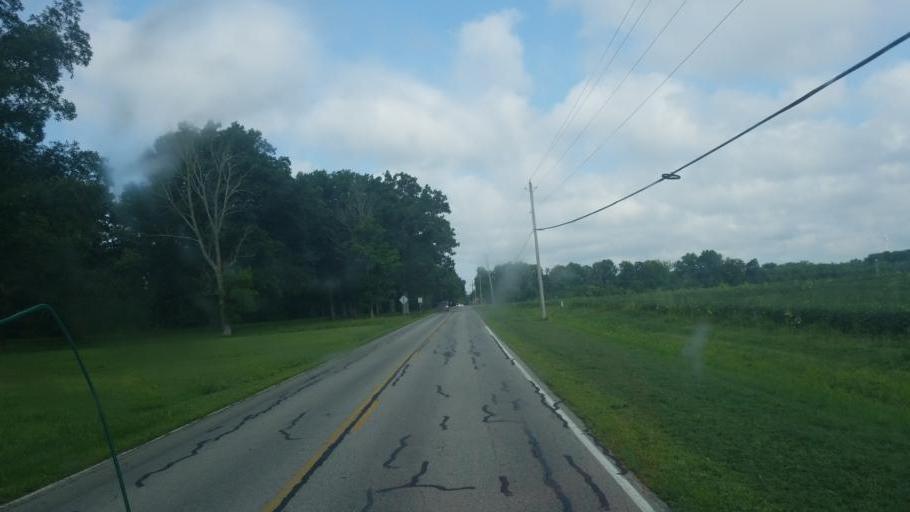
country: US
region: Ohio
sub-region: Marion County
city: Marion
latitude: 40.5716
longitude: -83.0890
